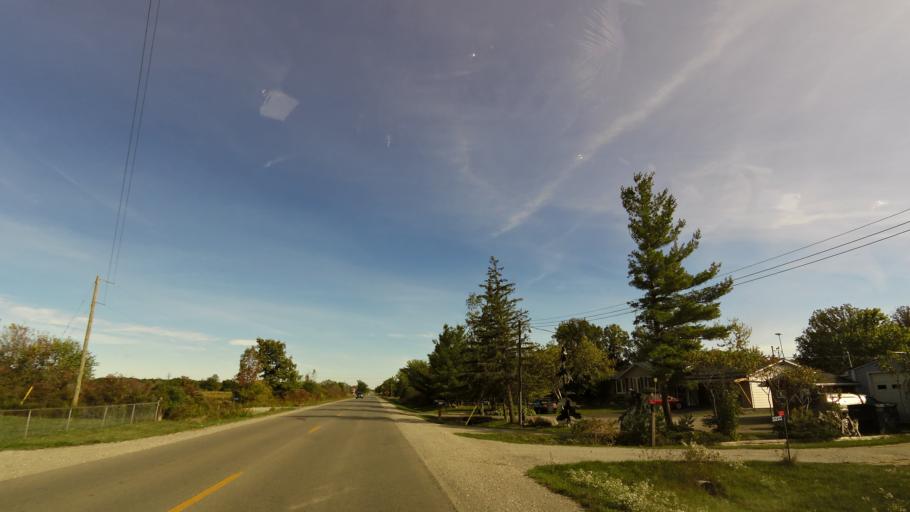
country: CA
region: Ontario
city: Ancaster
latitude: 43.0402
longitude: -80.0410
